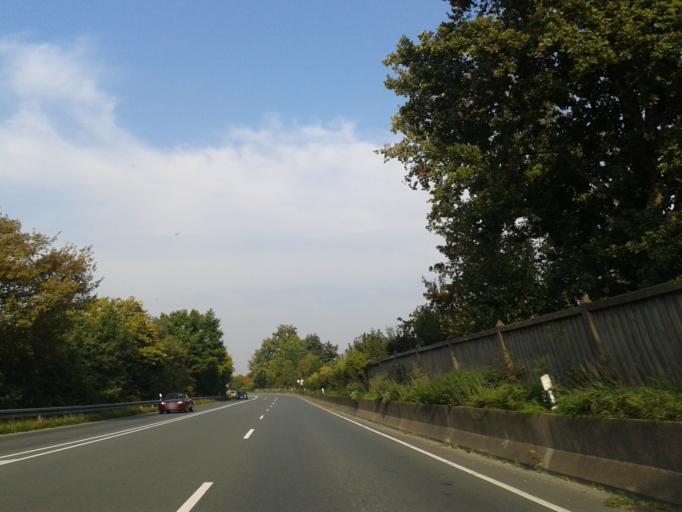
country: DE
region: North Rhine-Westphalia
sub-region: Regierungsbezirk Detmold
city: Hovelhof
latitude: 51.7570
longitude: 8.6594
